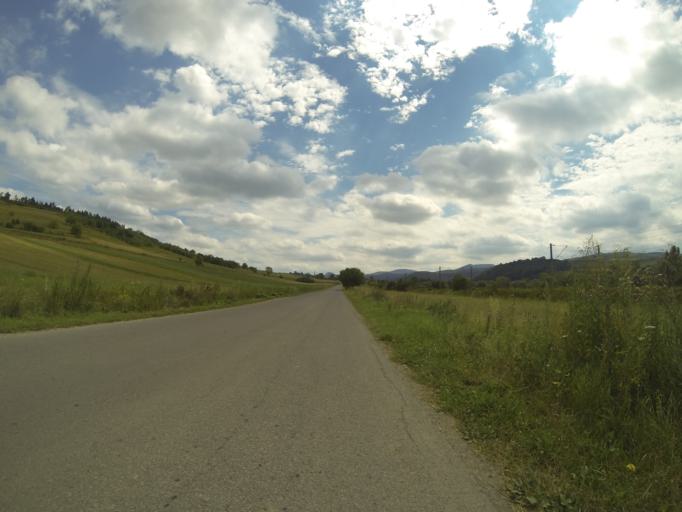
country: RO
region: Brasov
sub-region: Comuna Hoghiz
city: Hoghiz
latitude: 46.0279
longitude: 25.3913
